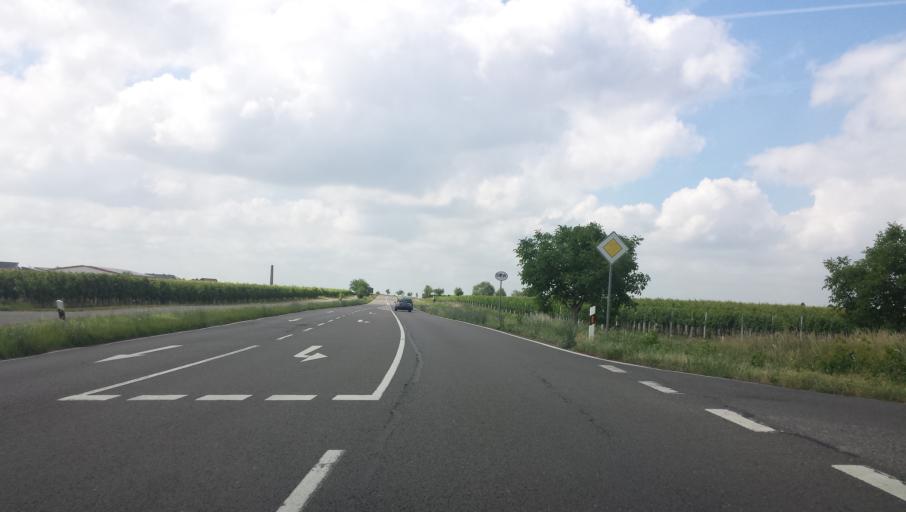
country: DE
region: Rheinland-Pfalz
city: Maikammer
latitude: 49.3127
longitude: 8.1443
